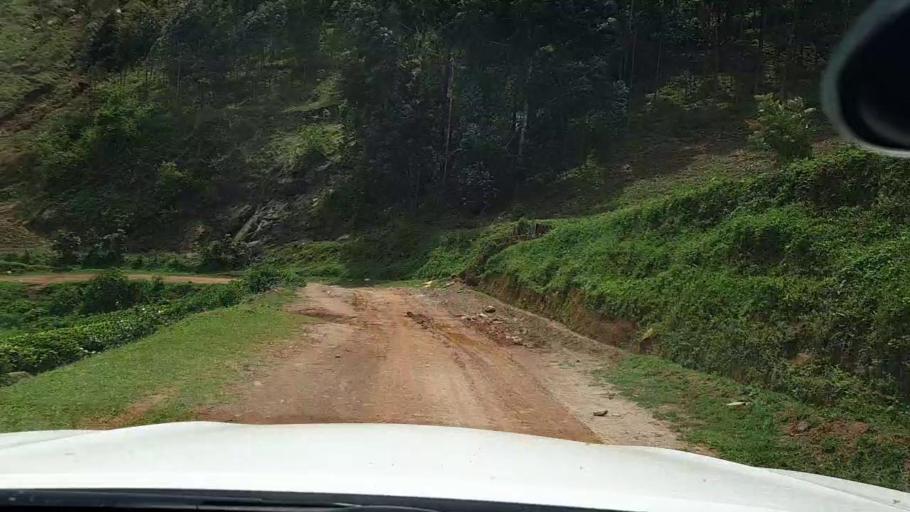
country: RW
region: Western Province
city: Kibuye
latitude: -2.1657
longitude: 29.4008
